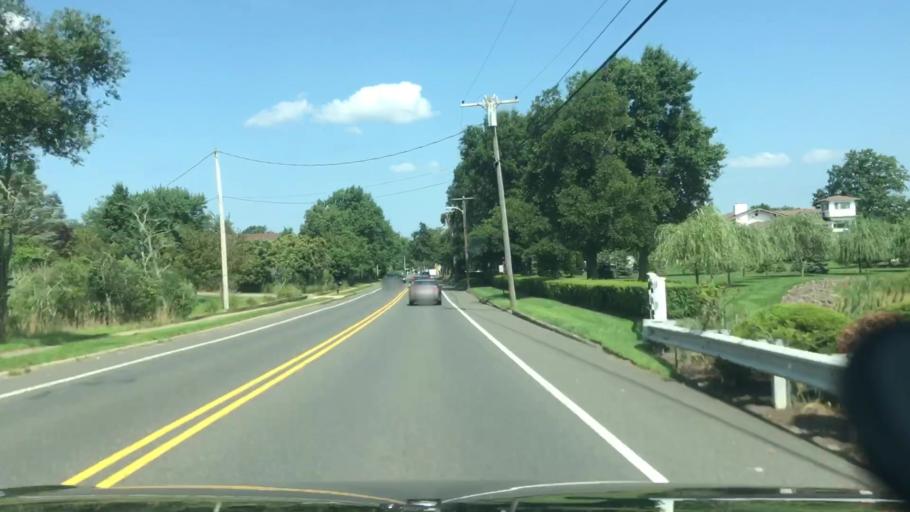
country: US
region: New Jersey
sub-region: Monmouth County
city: Oceanport
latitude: 40.3319
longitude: -74.0257
